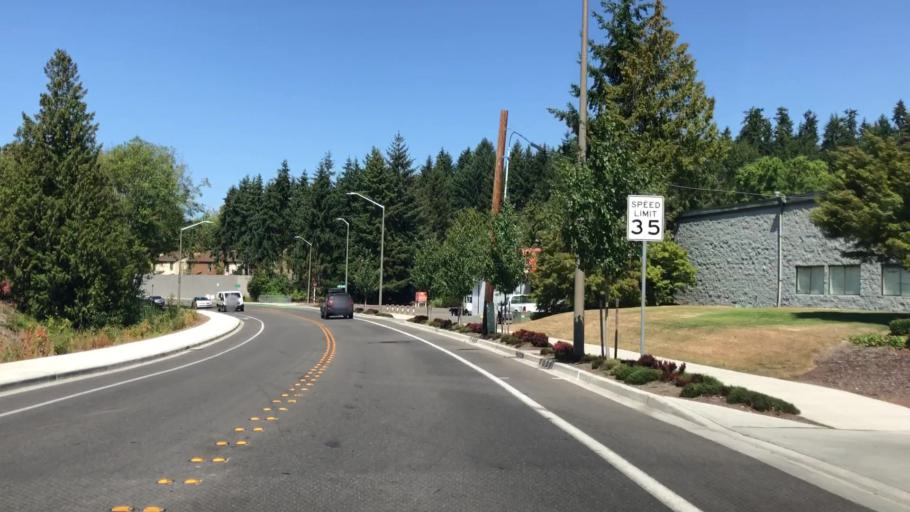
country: US
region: Washington
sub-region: King County
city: Yarrow Point
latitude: 47.6400
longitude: -122.1931
